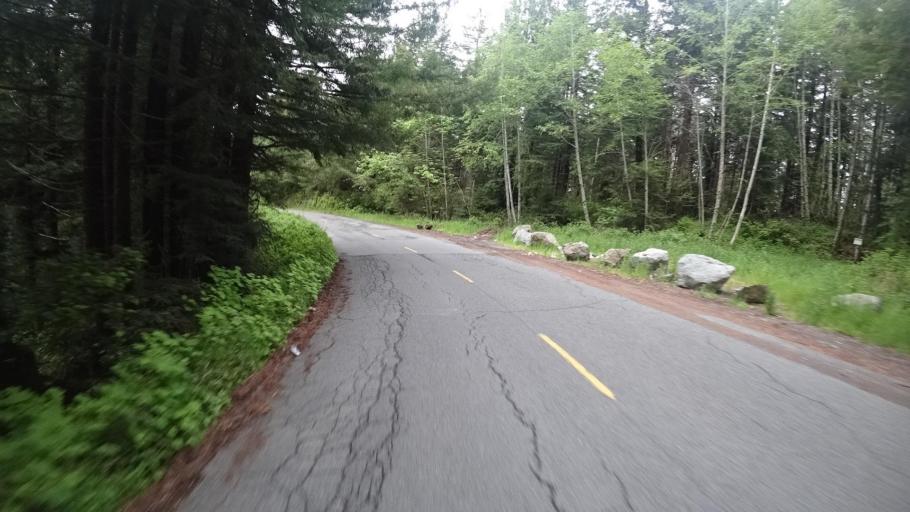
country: US
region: California
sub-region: Humboldt County
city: Blue Lake
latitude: 40.8796
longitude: -123.9709
